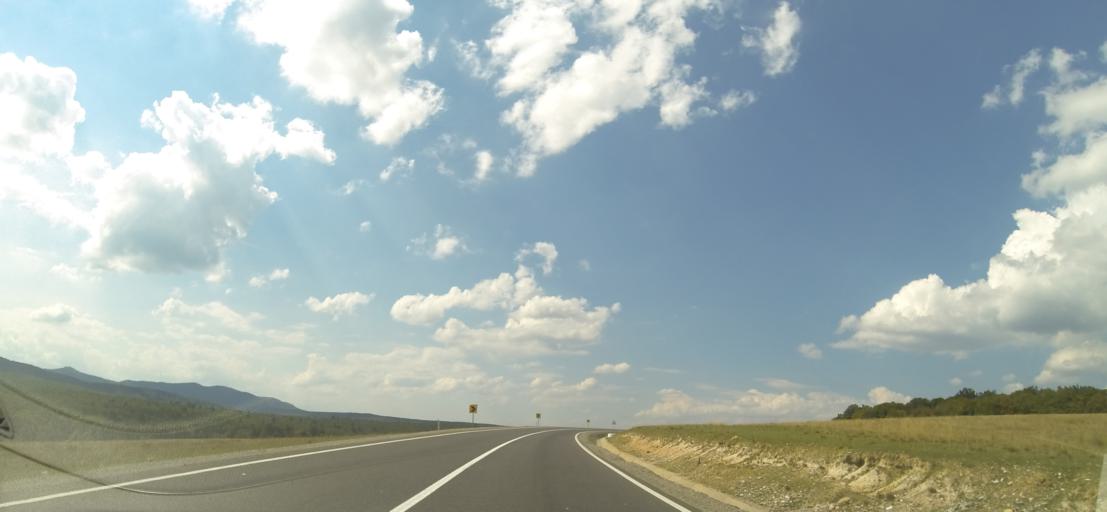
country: RO
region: Brasov
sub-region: Comuna Dumbravita
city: Dumbravita
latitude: 45.7490
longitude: 25.4078
